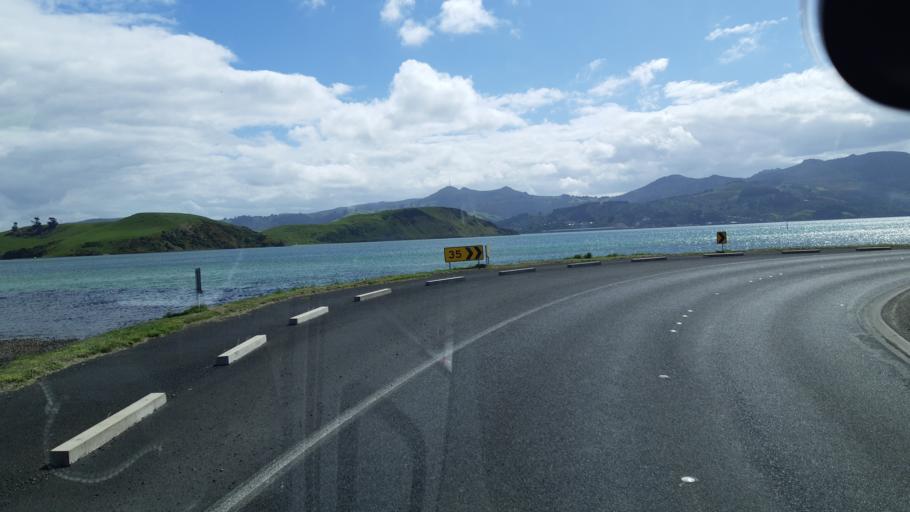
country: NZ
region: Otago
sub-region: Dunedin City
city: Portobello
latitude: -45.8301
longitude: 170.6715
